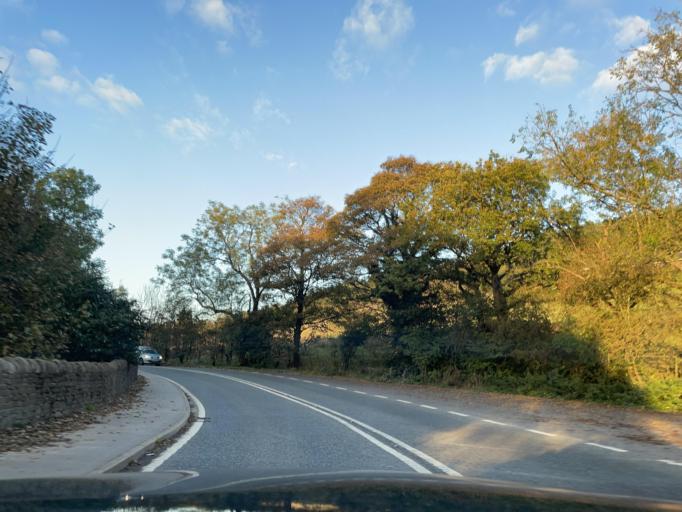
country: GB
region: England
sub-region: Borough of Stockport
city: Marple
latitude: 53.4171
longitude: -2.0317
